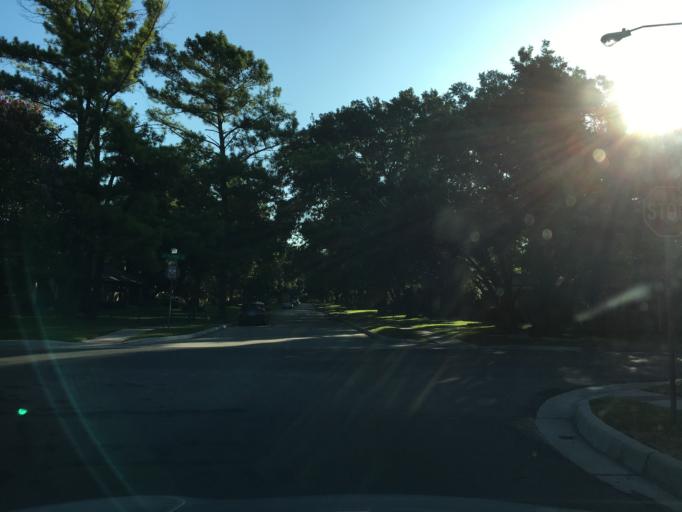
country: US
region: Texas
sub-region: Dallas County
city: Highland Park
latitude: 32.8583
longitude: -96.7379
